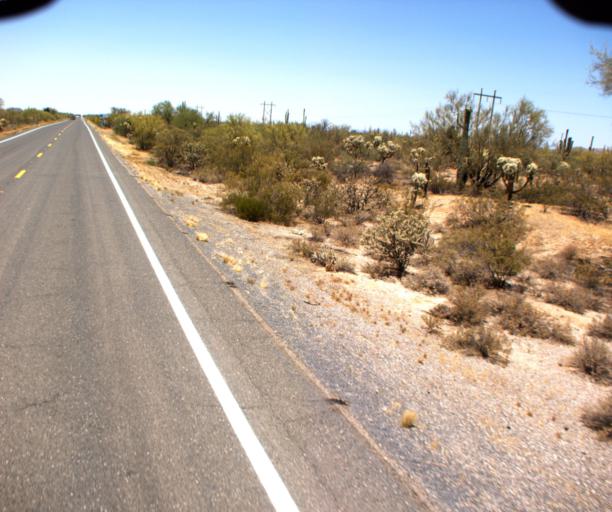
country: US
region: Arizona
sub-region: Pinal County
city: Florence
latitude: 32.8371
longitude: -111.2180
